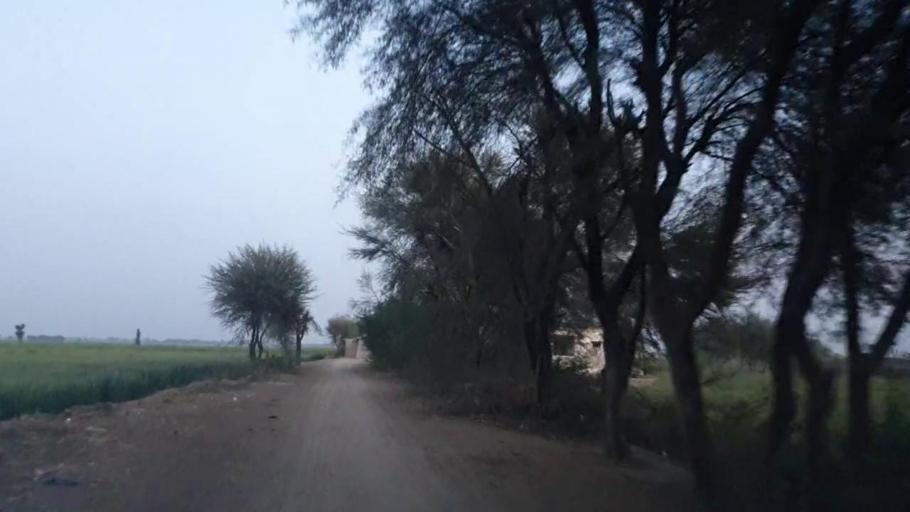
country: PK
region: Sindh
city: Naukot
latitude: 25.0214
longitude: 69.4110
